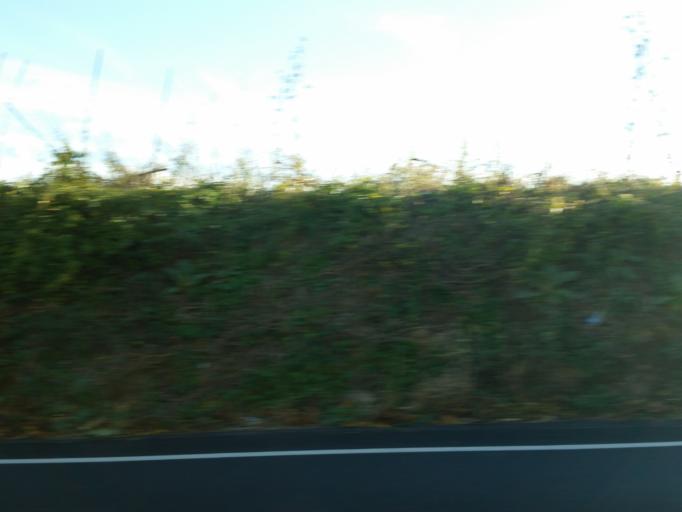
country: US
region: Pennsylvania
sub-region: Lebanon County
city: Cleona
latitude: 40.3448
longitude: -76.4802
